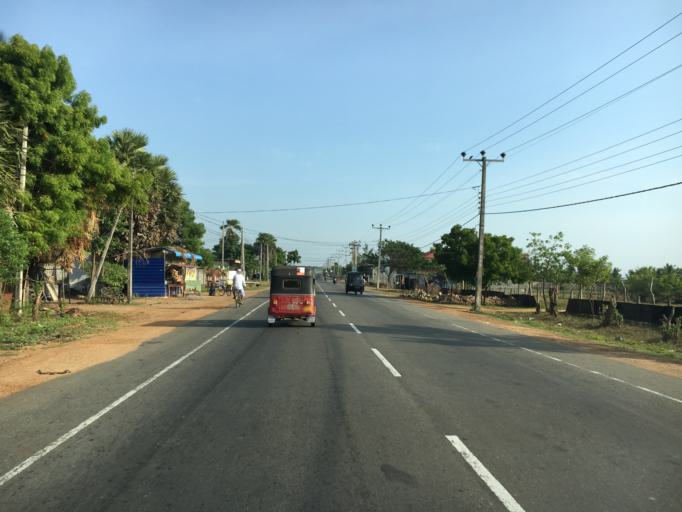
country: LK
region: Eastern Province
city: Eravur Town
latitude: 7.9301
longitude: 81.5124
